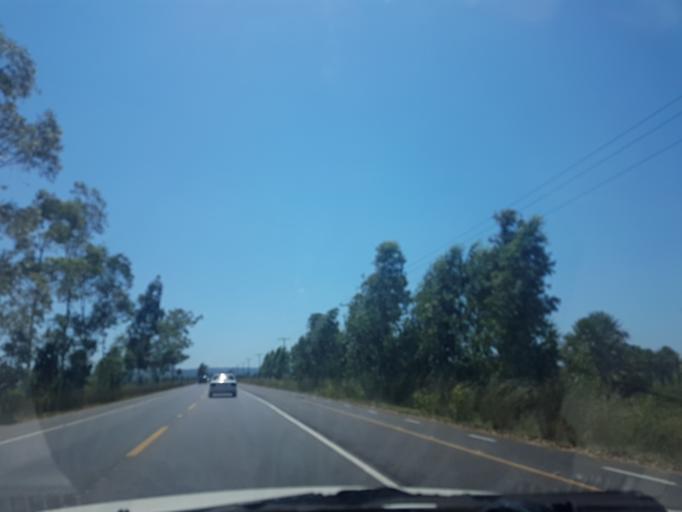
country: PY
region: Cordillera
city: Emboscada
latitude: -25.2094
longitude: -57.4071
